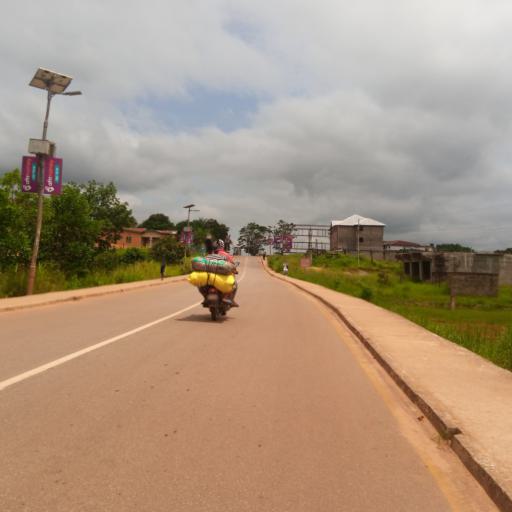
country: SL
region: Eastern Province
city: Kenema
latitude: 7.8544
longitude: -11.2058
